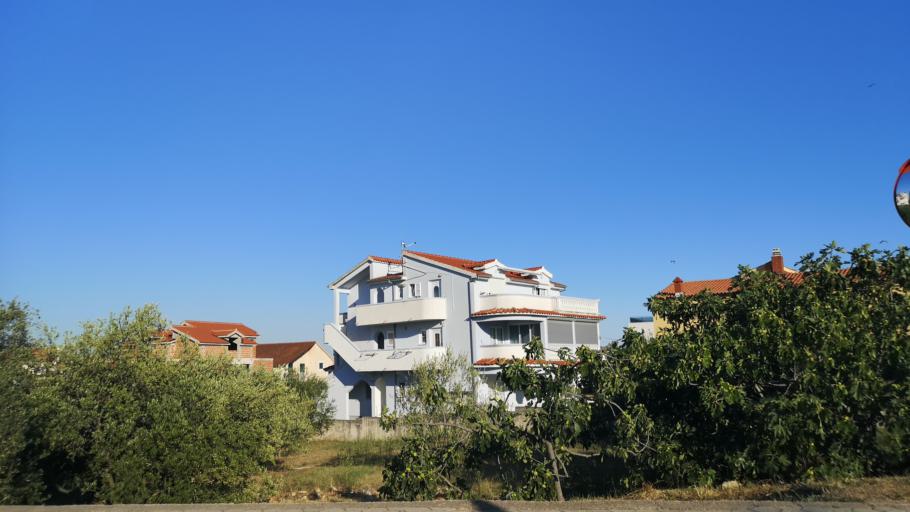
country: HR
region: Sibensko-Kniniska
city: Vodice
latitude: 43.7625
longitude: 15.7721
